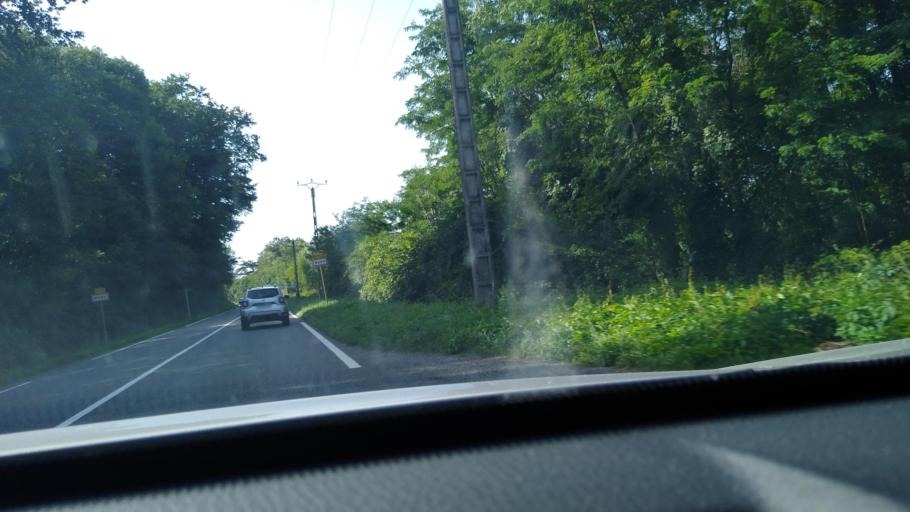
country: FR
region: Midi-Pyrenees
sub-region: Departement de la Haute-Garonne
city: Salies-du-Salat
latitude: 43.0776
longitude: 0.9584
